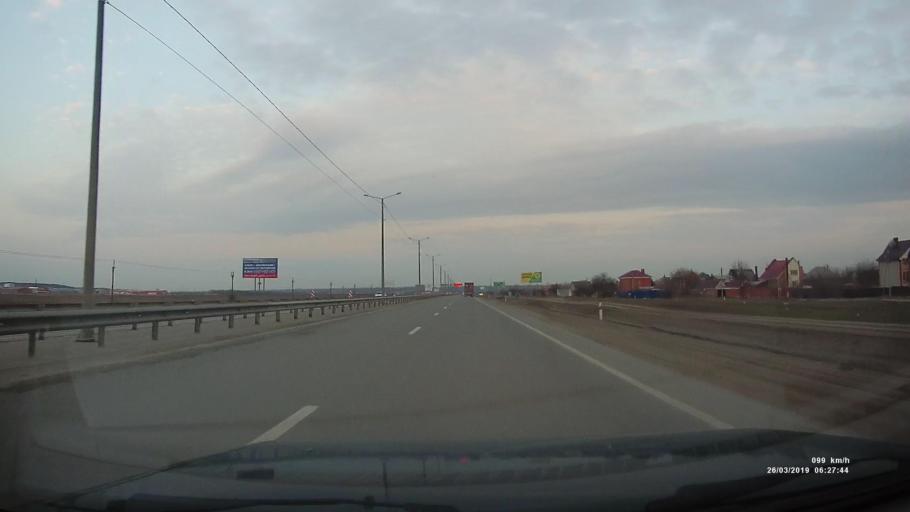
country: RU
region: Rostov
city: Kalinin
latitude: 47.2626
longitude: 39.6084
